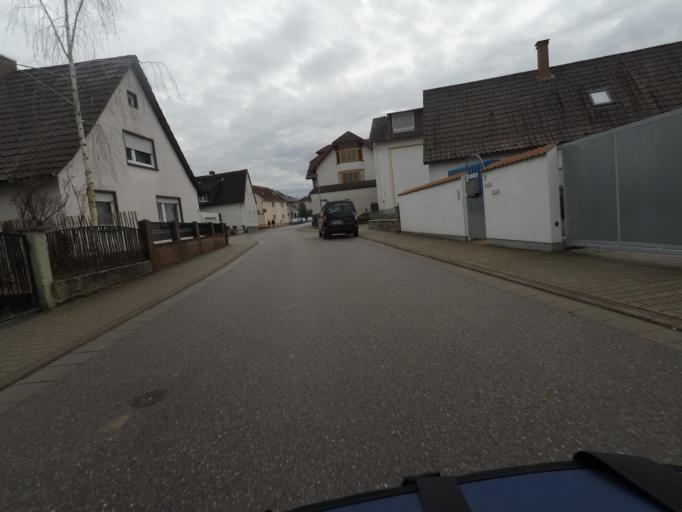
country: DE
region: Baden-Wuerttemberg
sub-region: Karlsruhe Region
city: Rheinstetten
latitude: 48.9731
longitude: 8.3061
